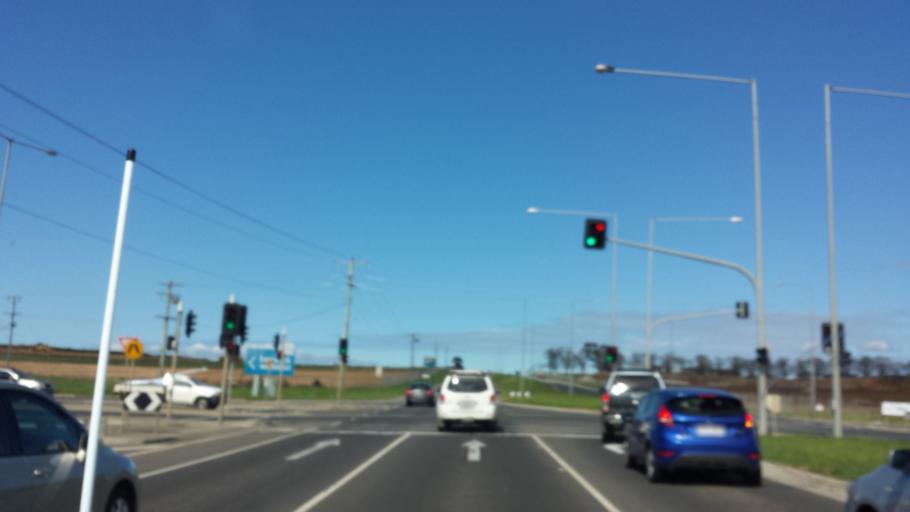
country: AU
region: Victoria
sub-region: Casey
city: Berwick
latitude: -38.0740
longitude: 145.3357
